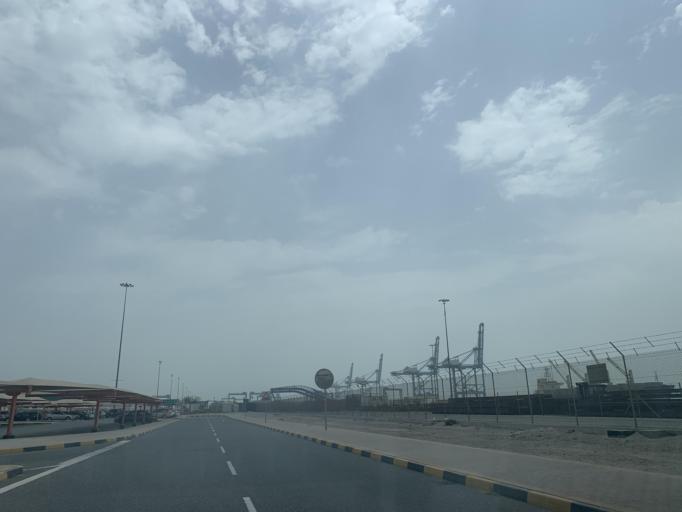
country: BH
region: Muharraq
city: Al Hadd
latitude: 26.1953
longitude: 50.7113
